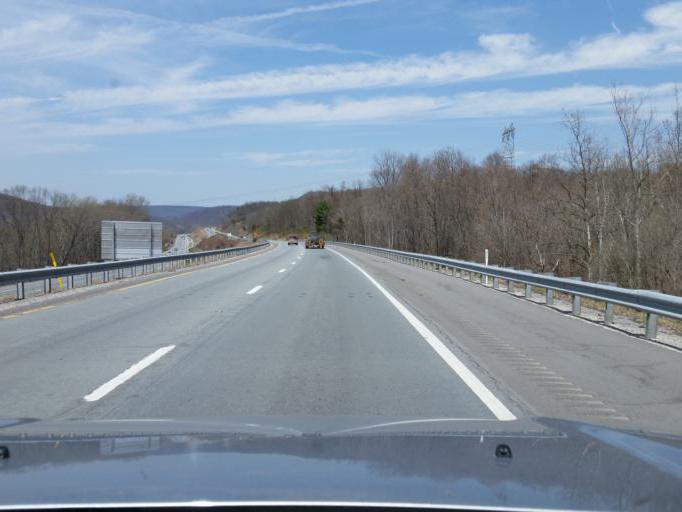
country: US
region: Pennsylvania
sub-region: Perry County
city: Duncannon
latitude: 40.4431
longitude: -77.0159
